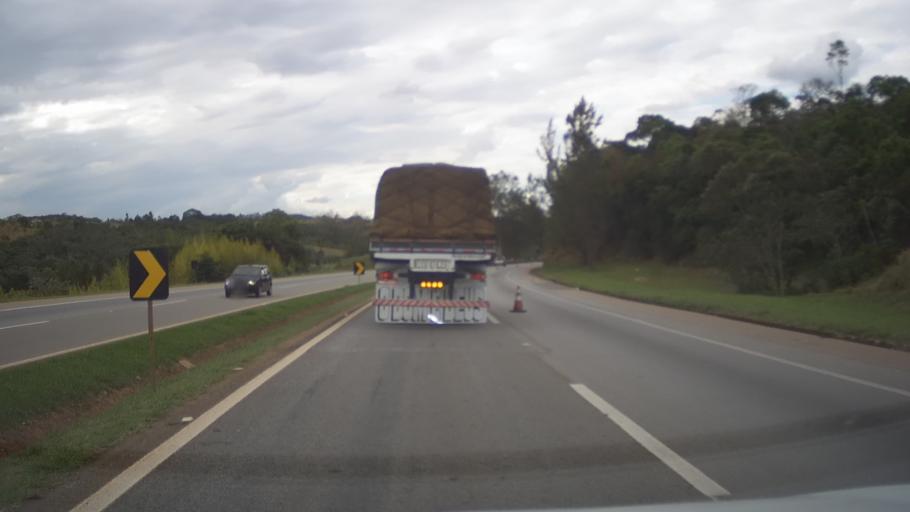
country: BR
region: Minas Gerais
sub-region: Itauna
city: Itauna
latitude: -20.3272
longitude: -44.4558
